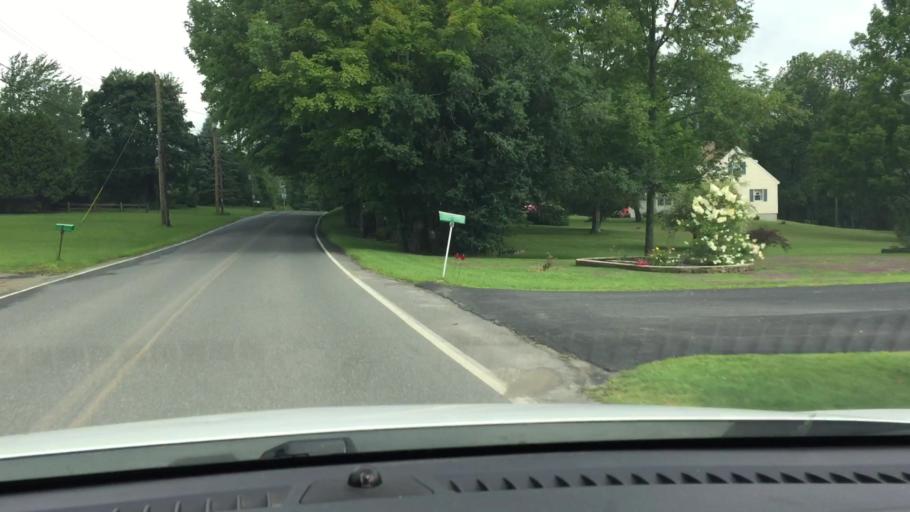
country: US
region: Massachusetts
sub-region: Berkshire County
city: Hinsdale
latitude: 42.4396
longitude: -73.1343
